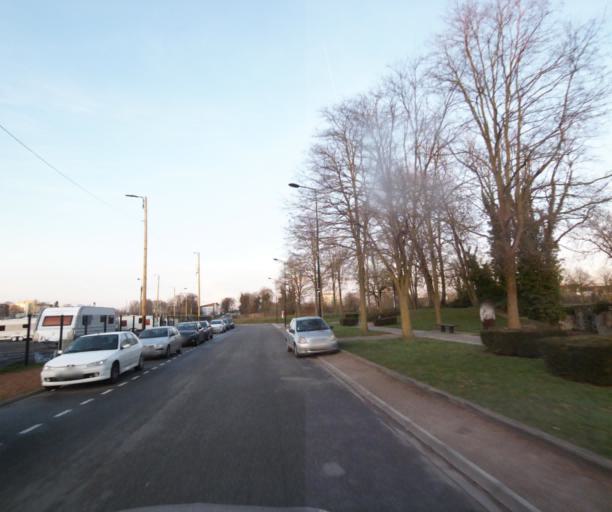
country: FR
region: Nord-Pas-de-Calais
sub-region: Departement du Nord
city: Anzin
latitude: 50.3565
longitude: 3.5139
